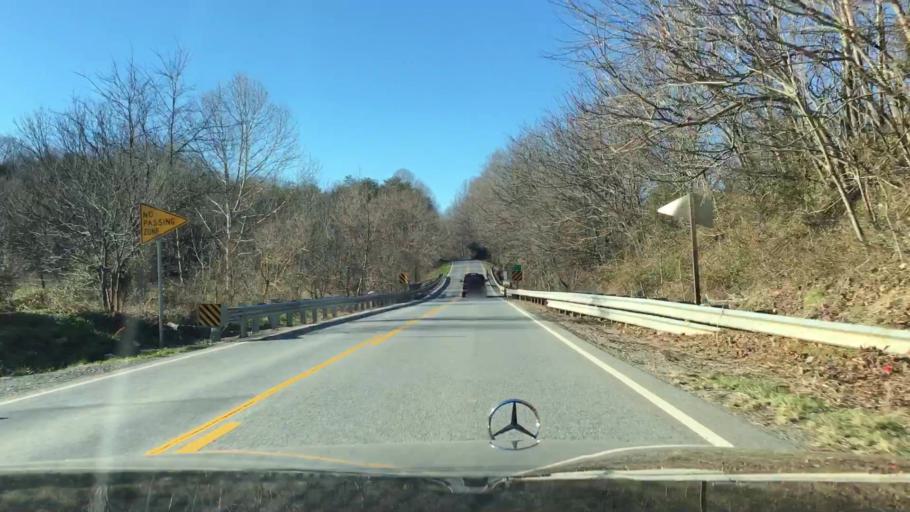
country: US
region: Virginia
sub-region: Botetourt County
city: Blue Ridge
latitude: 37.2608
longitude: -79.7471
